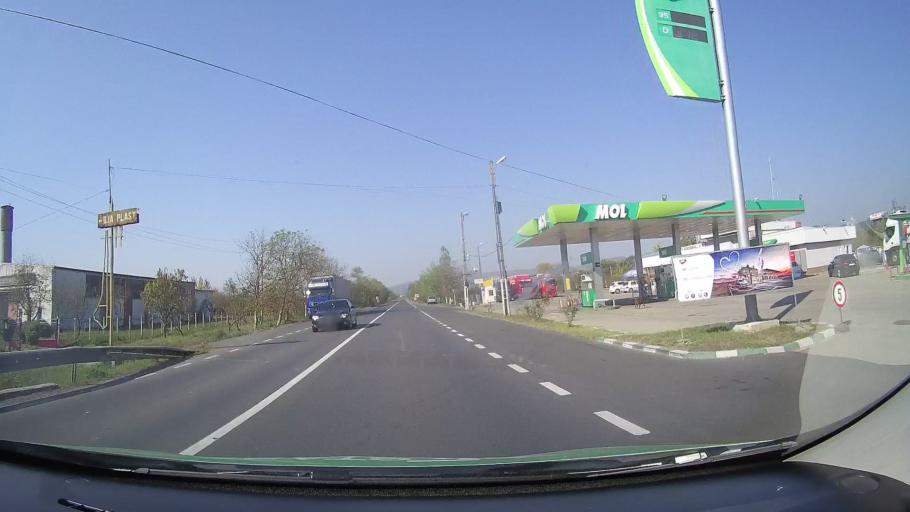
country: RO
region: Hunedoara
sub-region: Comuna Ilia
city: Ilia
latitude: 45.9405
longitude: 22.6458
